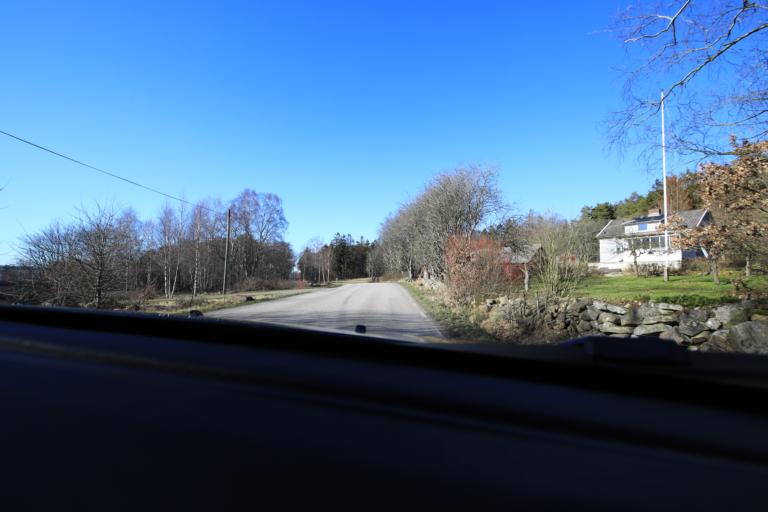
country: SE
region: Halland
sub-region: Varbergs Kommun
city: Tvaaker
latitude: 57.0622
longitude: 12.4247
